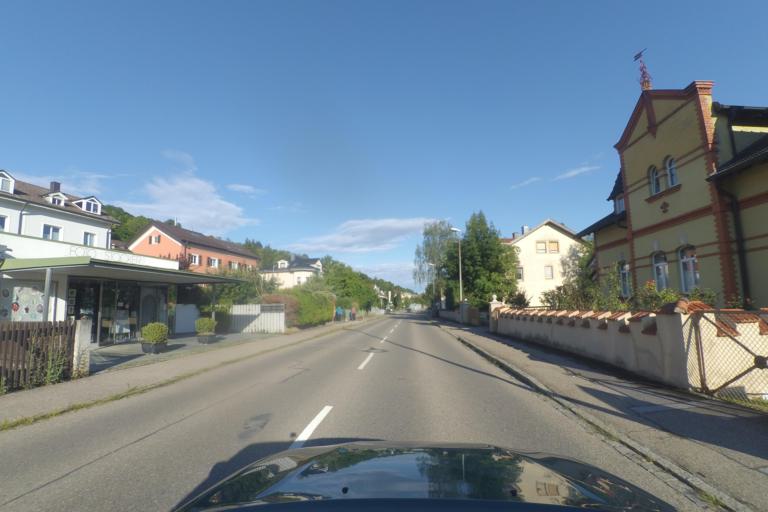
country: DE
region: Bavaria
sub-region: Upper Bavaria
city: Eichstaett
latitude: 48.8880
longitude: 11.1960
